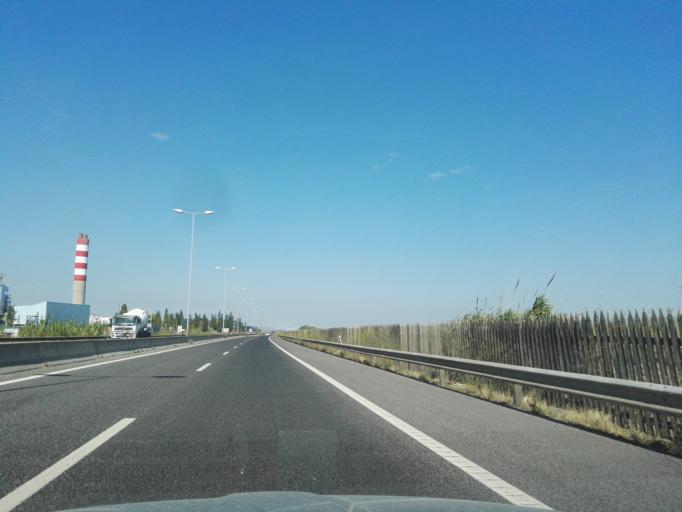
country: PT
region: Lisbon
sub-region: Loures
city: Sao Joao da Talha
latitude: 38.8245
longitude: -9.0836
